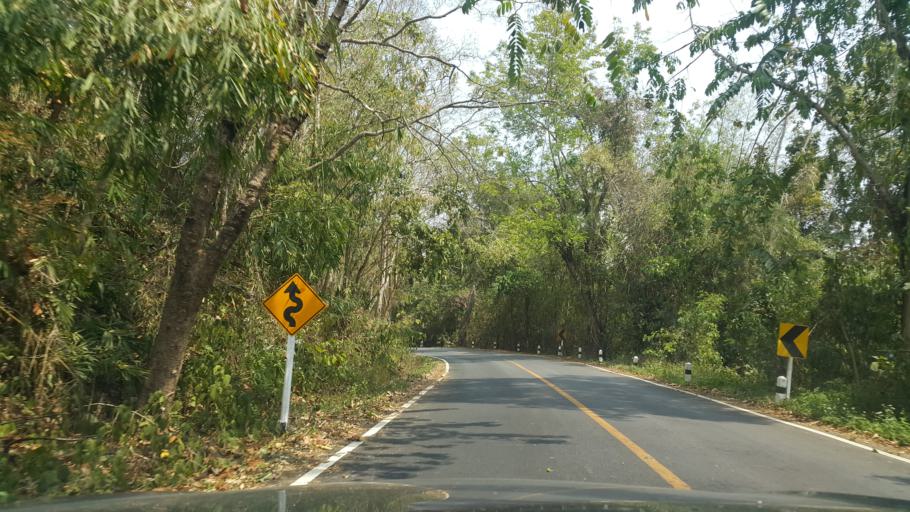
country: TH
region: Lamphun
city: Thung Hua Chang
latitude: 17.9054
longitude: 99.1206
